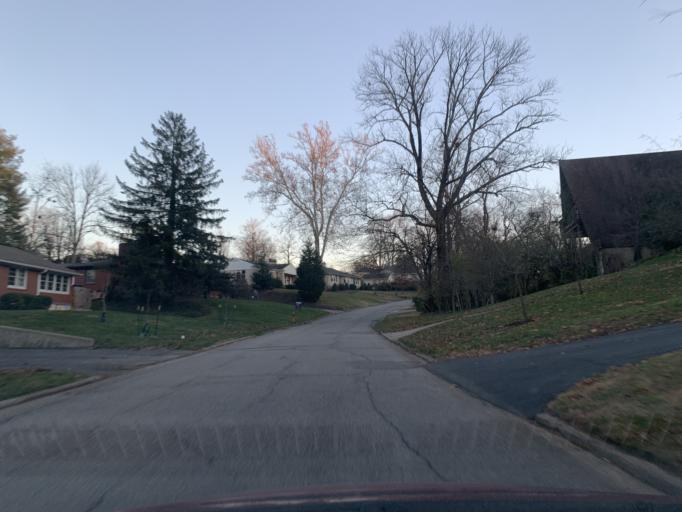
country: US
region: Kentucky
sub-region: Jefferson County
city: Saint Matthews
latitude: 38.2312
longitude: -85.6811
